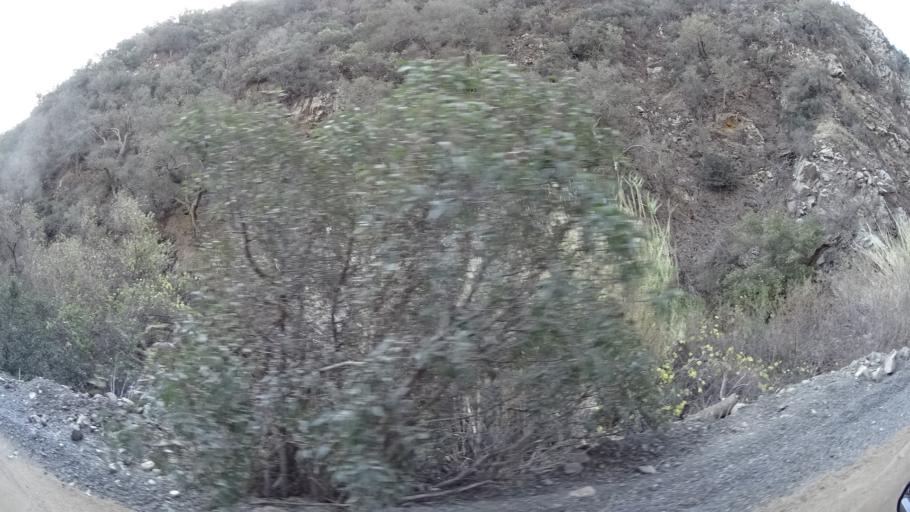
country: US
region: California
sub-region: Orange County
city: Trabuco Canyon
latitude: 33.6747
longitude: -117.5471
